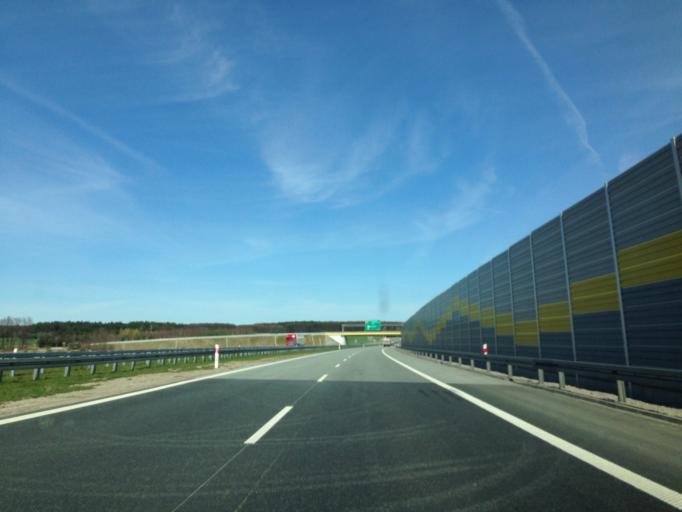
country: PL
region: Lodz Voivodeship
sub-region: Powiat sieradzki
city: Sieradz
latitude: 51.5874
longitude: 18.8080
